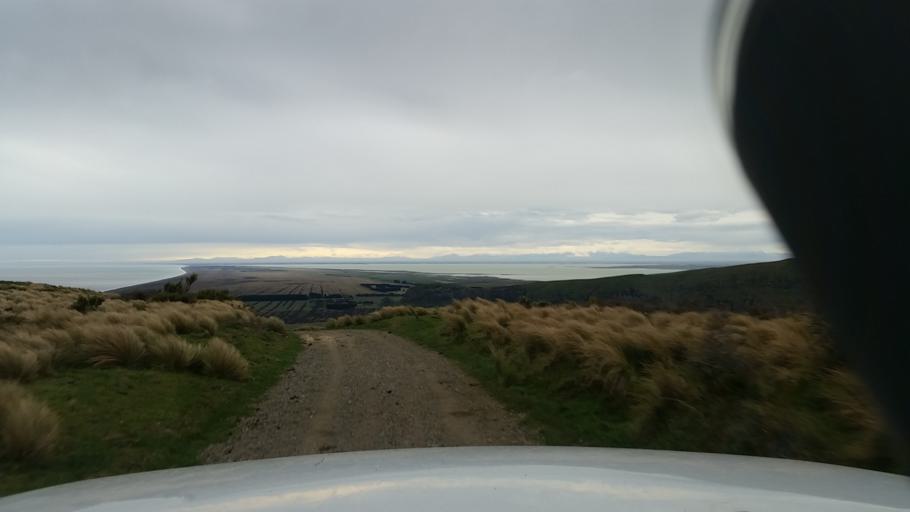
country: NZ
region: Canterbury
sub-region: Christchurch City
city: Christchurch
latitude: -43.8180
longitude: 172.7379
